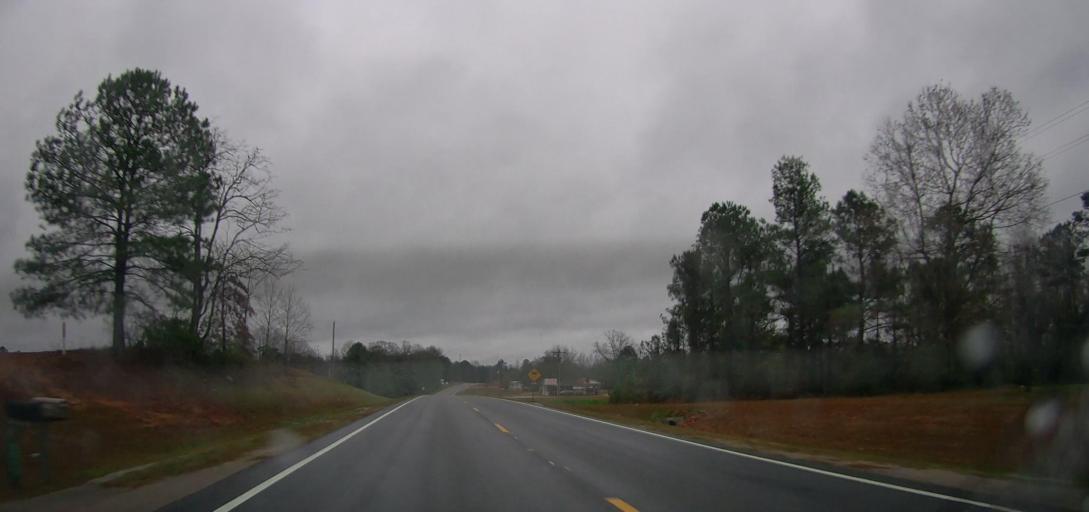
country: US
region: Alabama
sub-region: Chilton County
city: Thorsby
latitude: 32.8019
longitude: -86.9150
